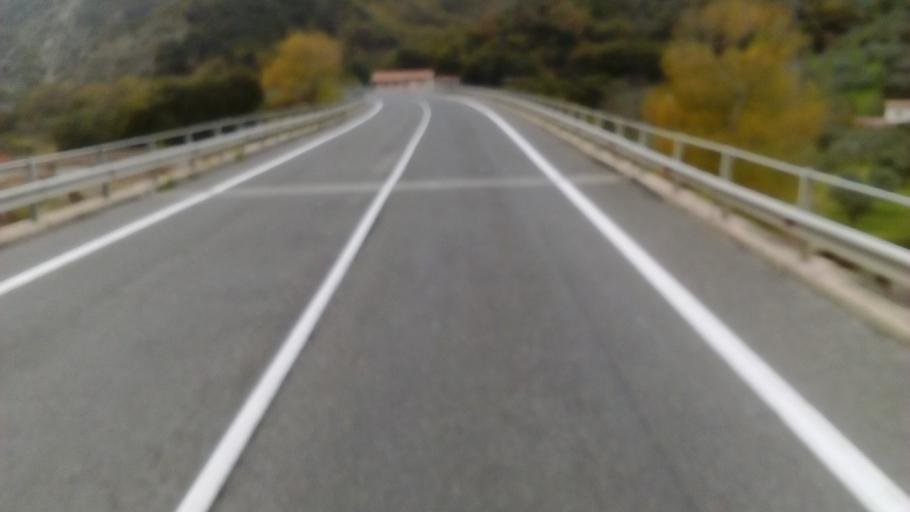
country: IT
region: Molise
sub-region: Provincia di Campobasso
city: Trivento
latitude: 41.7978
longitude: 14.5559
